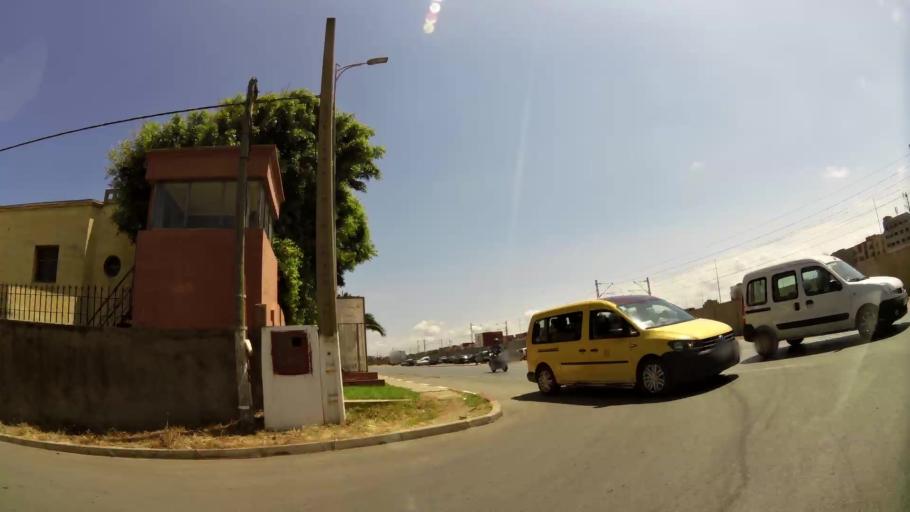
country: MA
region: Rabat-Sale-Zemmour-Zaer
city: Sale
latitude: 34.0794
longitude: -6.7787
